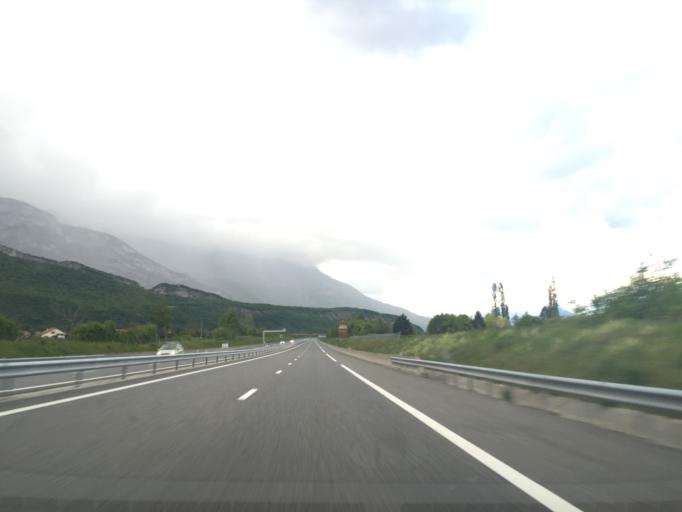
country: FR
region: Rhone-Alpes
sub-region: Departement de l'Isere
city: Vif
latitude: 45.0594
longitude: 5.6847
